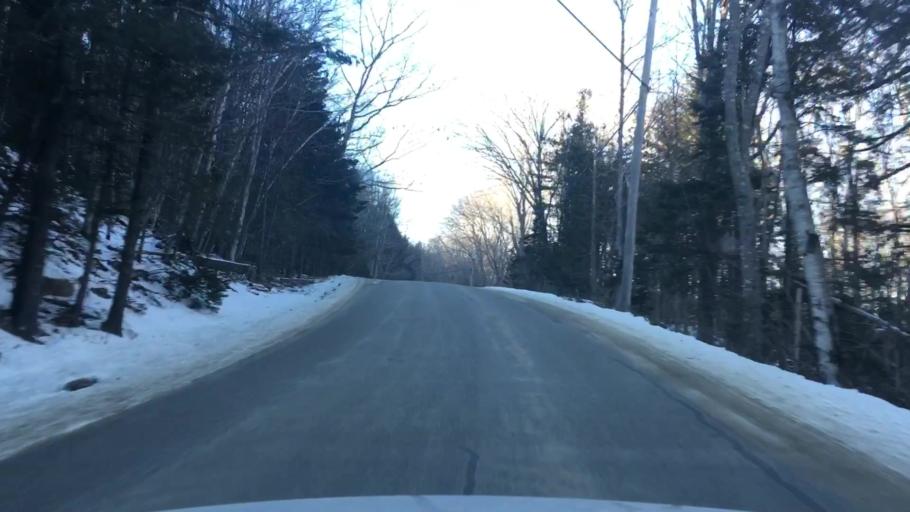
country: US
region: Maine
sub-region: Hancock County
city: Castine
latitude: 44.3459
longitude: -68.7822
